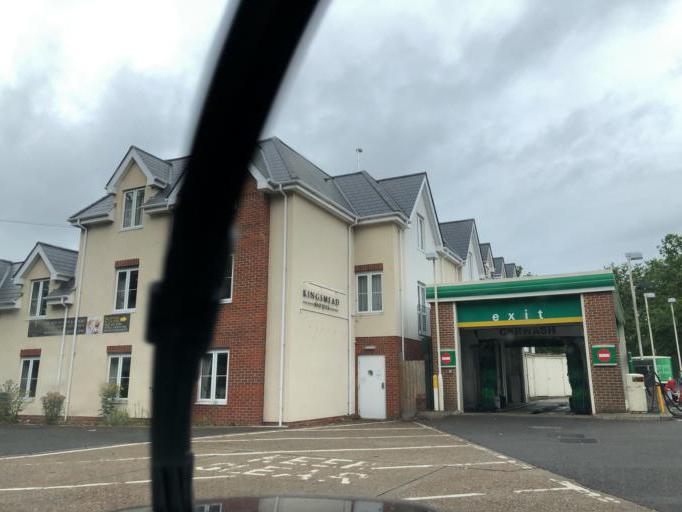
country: GB
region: England
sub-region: Hampshire
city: Farnborough
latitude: 51.2866
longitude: -0.7255
